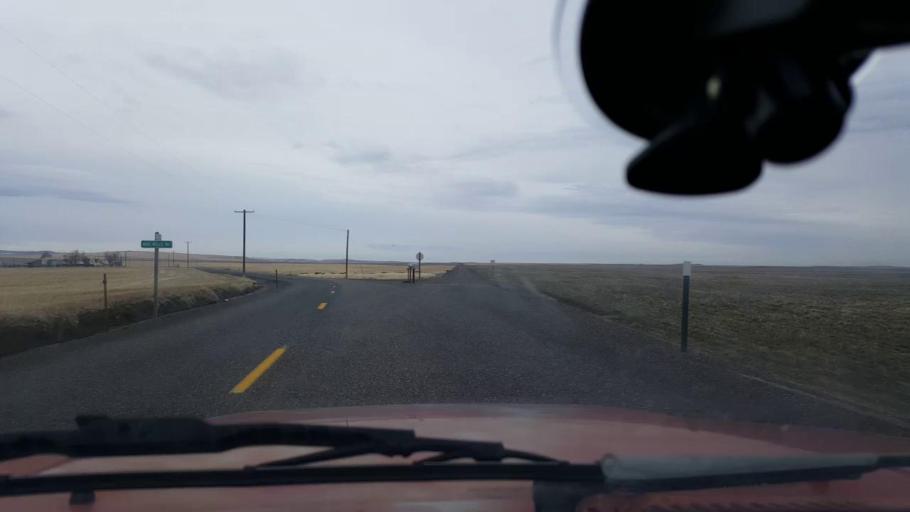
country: US
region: Washington
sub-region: Asotin County
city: Clarkston Heights-Vineland
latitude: 46.3748
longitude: -117.1637
